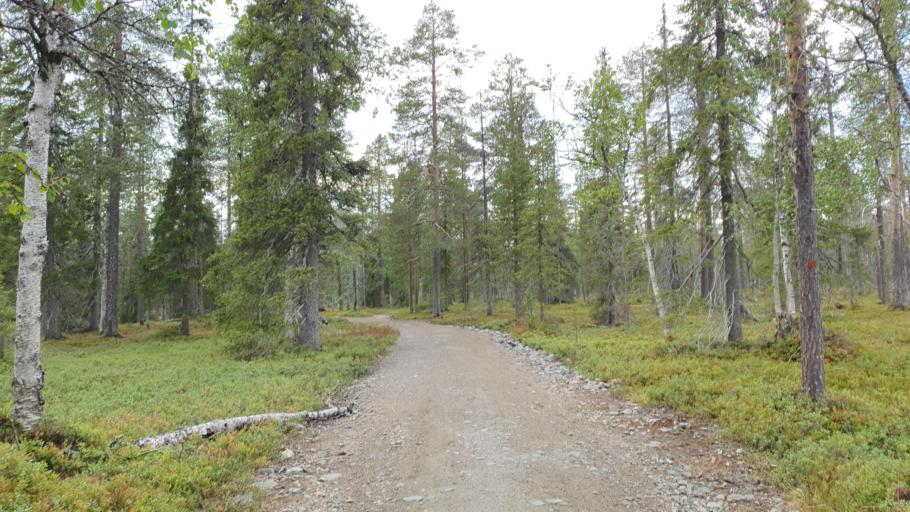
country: FI
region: Lapland
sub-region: Tunturi-Lappi
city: Kolari
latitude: 67.6190
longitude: 24.2303
